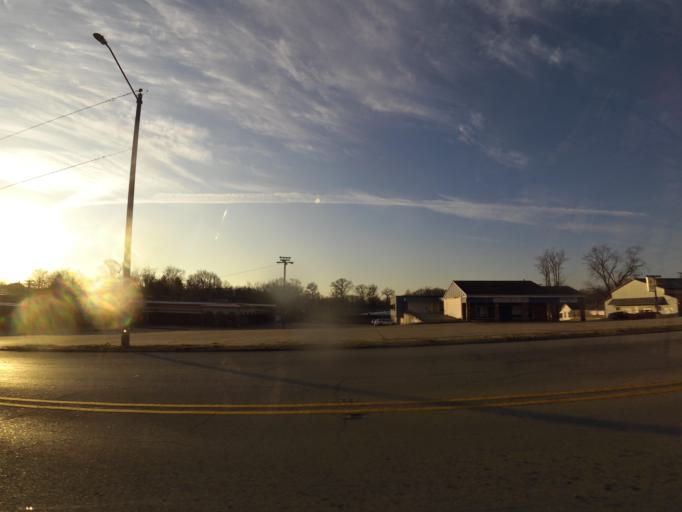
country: US
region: Illinois
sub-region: Fayette County
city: Vandalia
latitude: 38.9607
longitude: -89.0928
